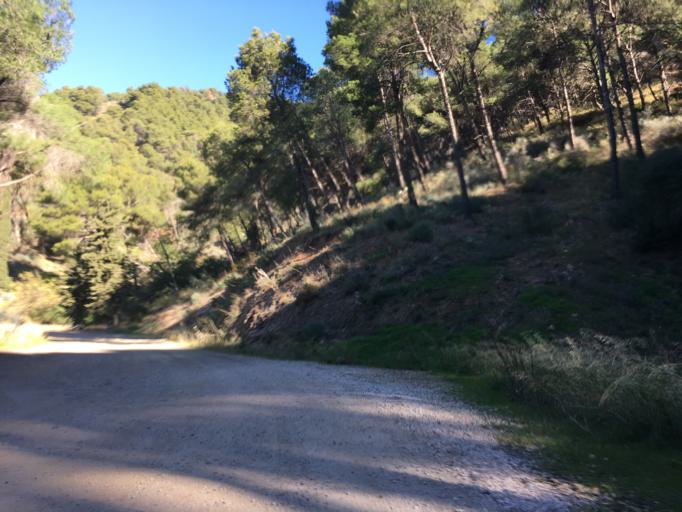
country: ES
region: Andalusia
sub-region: Provincia de Malaga
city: Malaga
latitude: 36.7767
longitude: -4.3840
